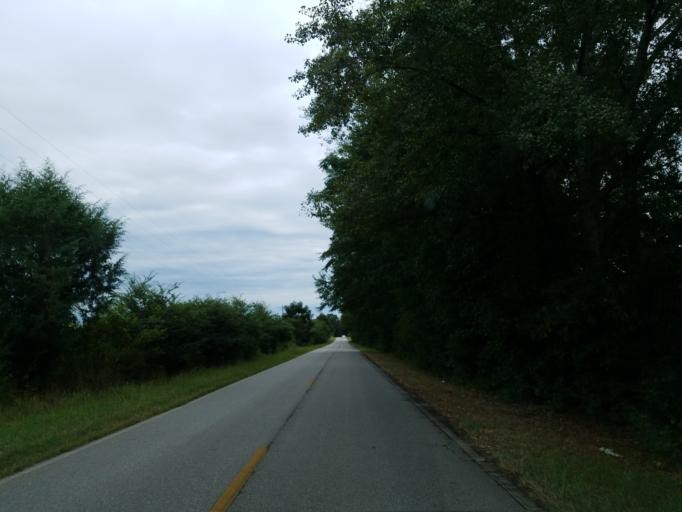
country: US
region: Georgia
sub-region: Lamar County
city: Barnesville
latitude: 33.0048
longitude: -84.0673
